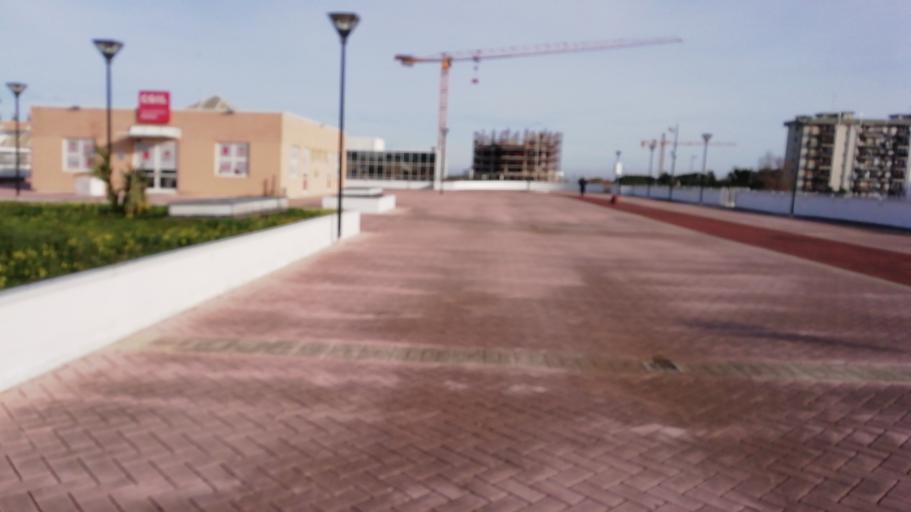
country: IT
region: Apulia
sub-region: Provincia di Bari
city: Triggiano
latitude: 41.1049
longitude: 16.9124
